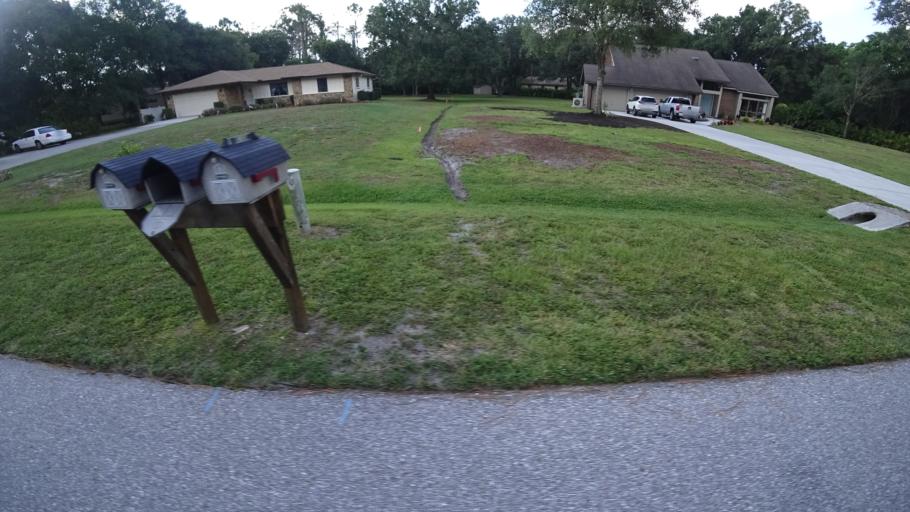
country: US
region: Florida
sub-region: Sarasota County
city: The Meadows
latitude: 27.4296
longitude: -82.4471
